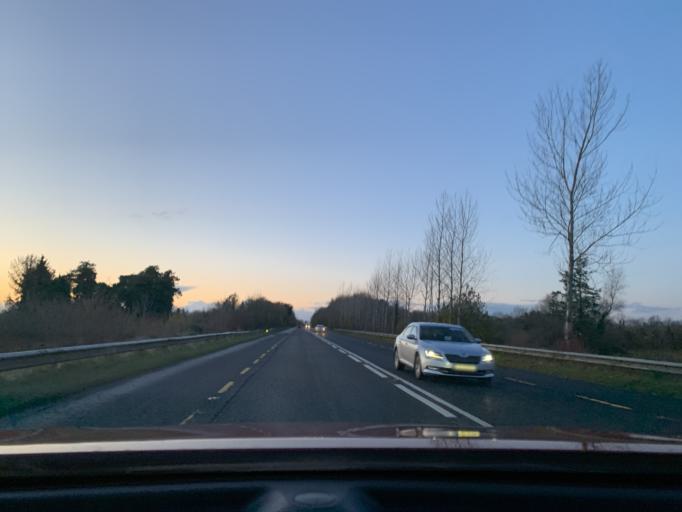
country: IE
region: Connaught
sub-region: County Leitrim
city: Carrick-on-Shannon
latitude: 53.9342
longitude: -8.0471
